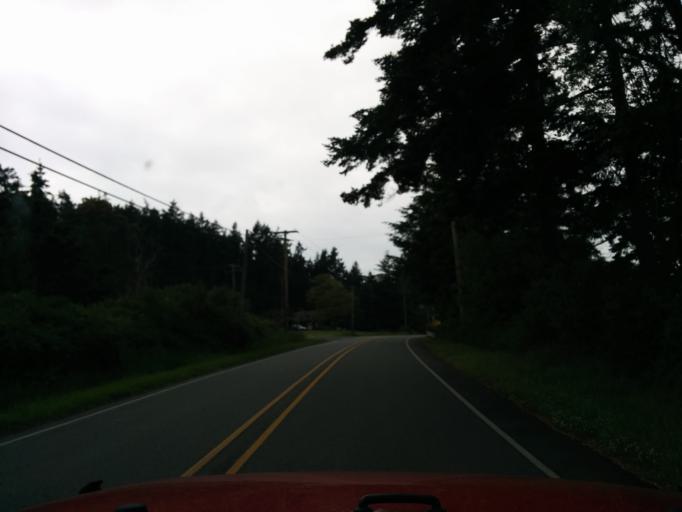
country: US
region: Washington
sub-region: Island County
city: Coupeville
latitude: 48.2165
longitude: -122.7024
